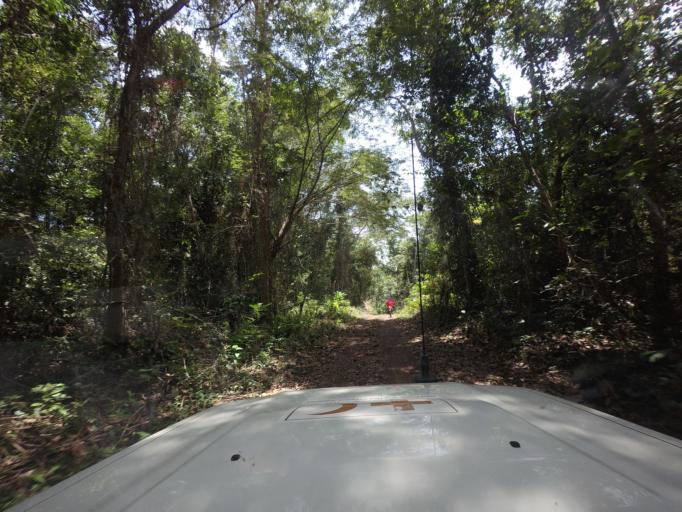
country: GN
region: Nzerekore
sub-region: Yomou
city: Yomou
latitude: 7.3746
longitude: -9.3125
